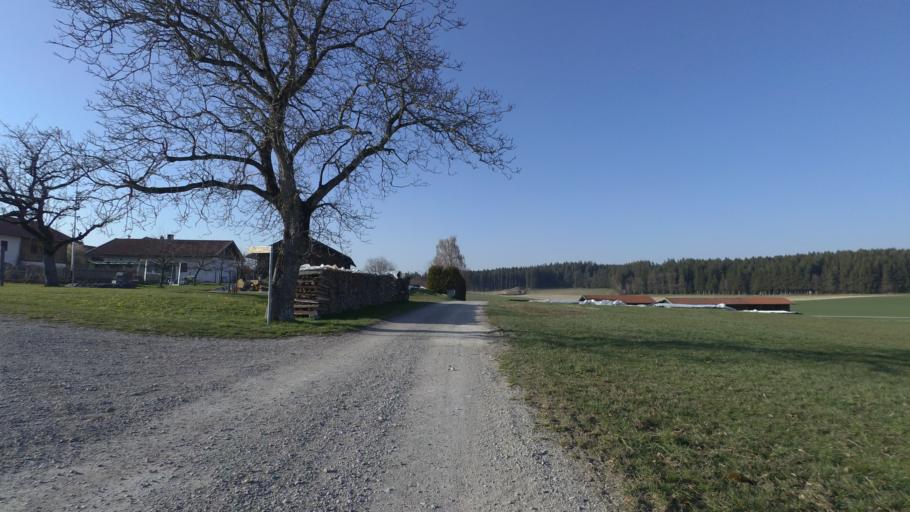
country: DE
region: Bavaria
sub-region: Upper Bavaria
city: Traunreut
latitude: 47.9383
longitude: 12.5584
